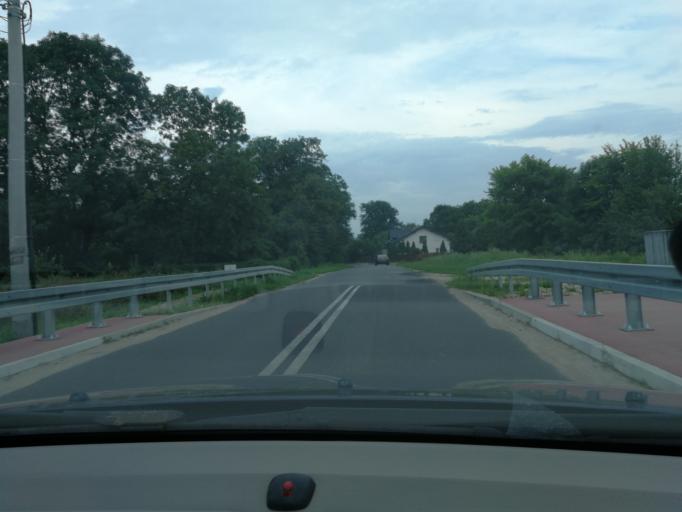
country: PL
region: Masovian Voivodeship
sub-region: Powiat grodziski
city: Grodzisk Mazowiecki
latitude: 52.1310
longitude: 20.5908
